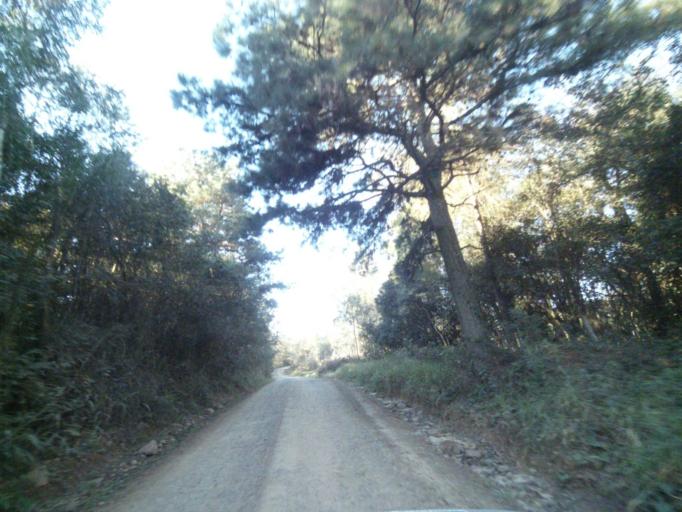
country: BR
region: Parana
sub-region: Tibagi
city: Tibagi
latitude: -24.5312
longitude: -50.5989
